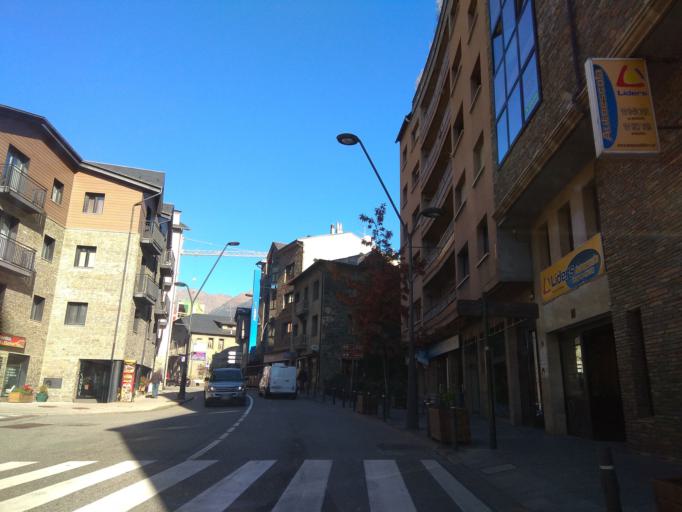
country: AD
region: La Massana
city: la Massana
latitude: 42.5453
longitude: 1.5152
